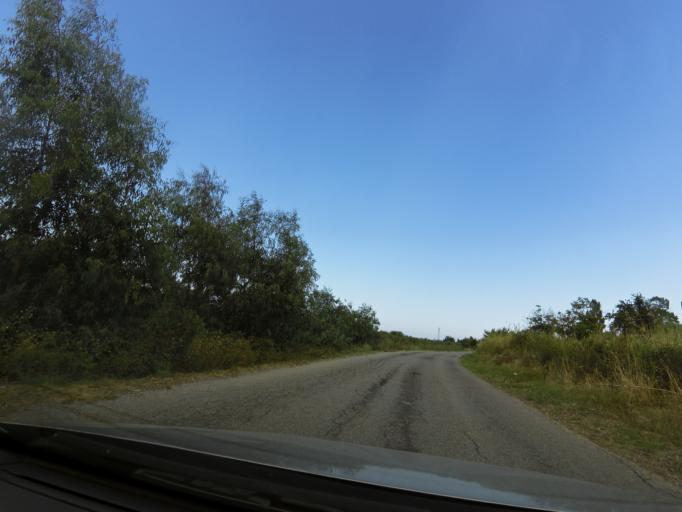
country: IT
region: Calabria
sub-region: Provincia di Reggio Calabria
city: Monasterace Marina
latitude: 38.4222
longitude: 16.5516
